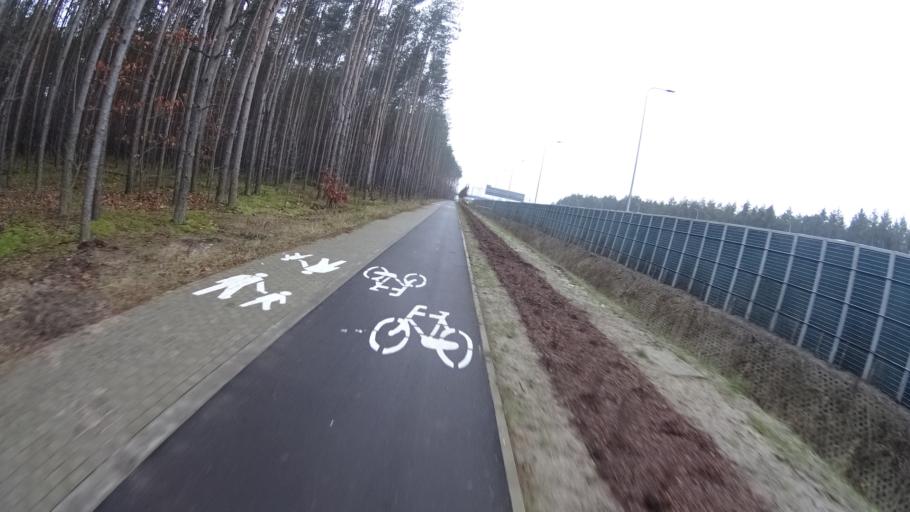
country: PL
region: Masovian Voivodeship
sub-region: Warszawa
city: Wawer
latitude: 52.1667
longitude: 21.1929
